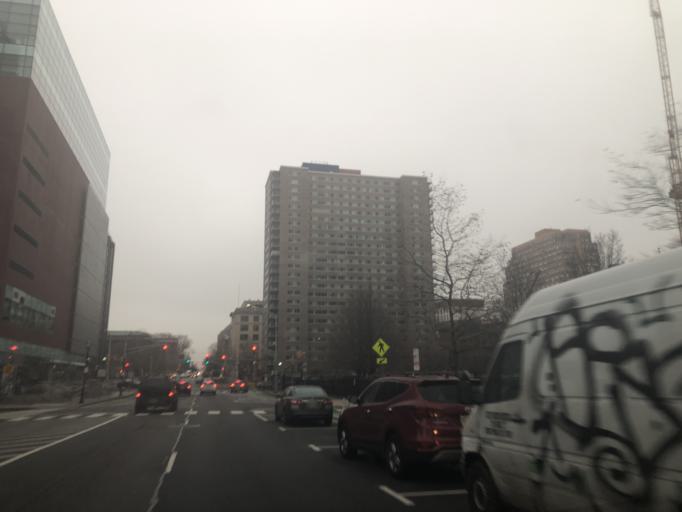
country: US
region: New Jersey
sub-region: Hudson County
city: Hoboken
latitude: 40.7187
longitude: -74.0370
